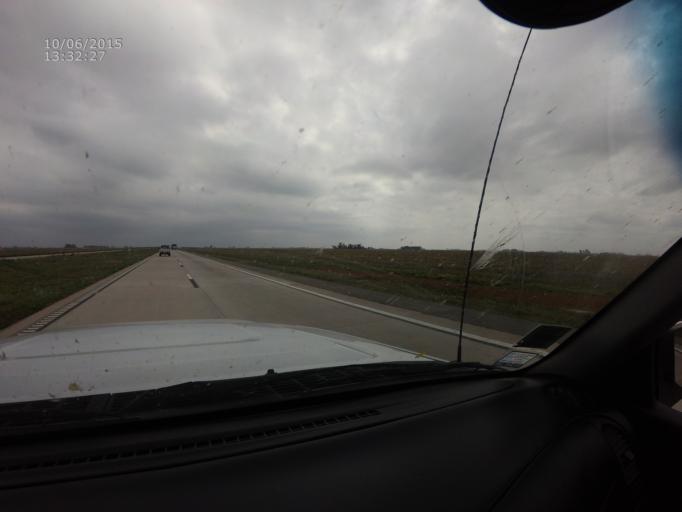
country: AR
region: Cordoba
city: Leones
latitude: -32.6270
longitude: -62.3075
